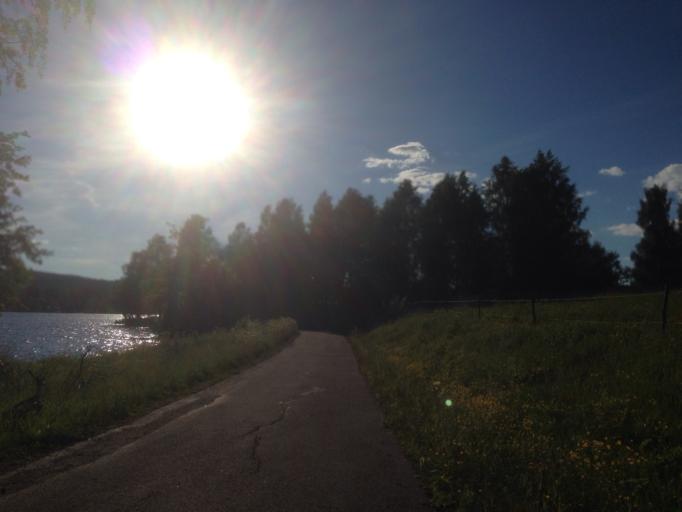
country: SE
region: Dalarna
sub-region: Ludvika Kommun
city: Ludvika
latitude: 60.1049
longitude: 15.2141
